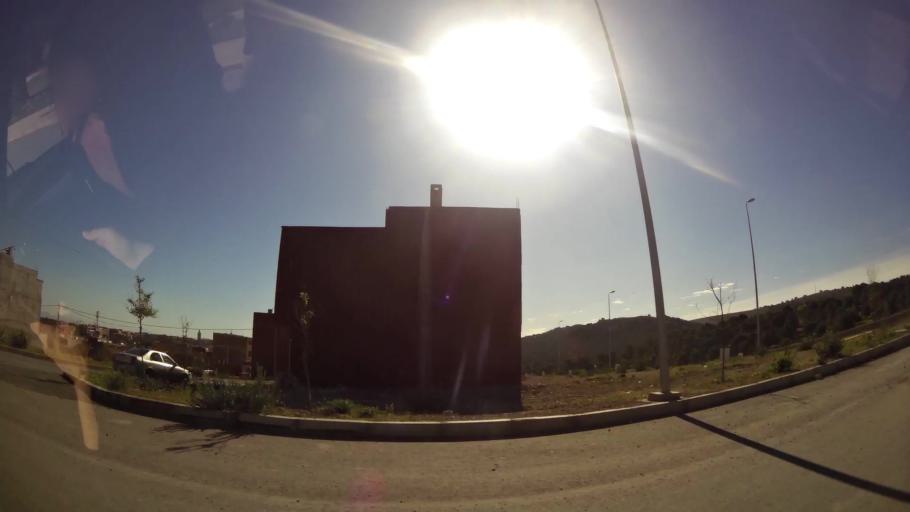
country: MA
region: Oriental
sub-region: Oujda-Angad
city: Oujda
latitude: 34.6453
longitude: -1.8886
